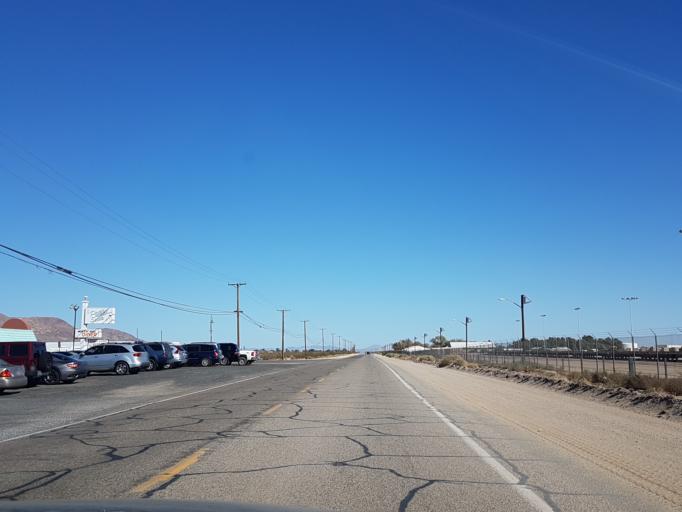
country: US
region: California
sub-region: San Bernardino County
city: Barstow
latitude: 34.9011
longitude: -116.8840
